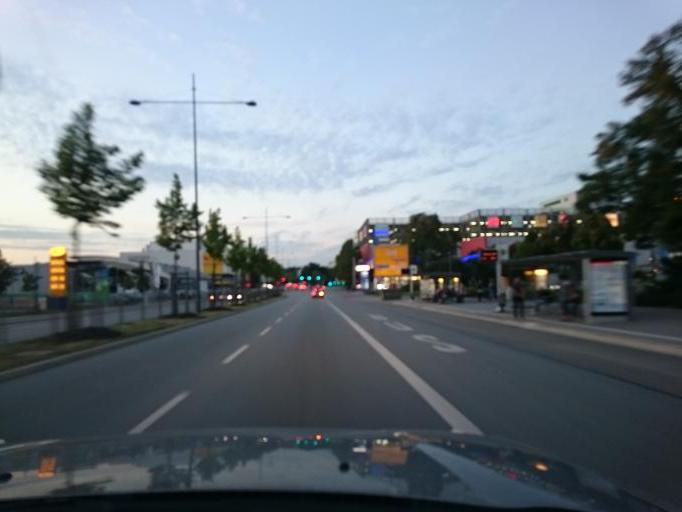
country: DE
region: Bavaria
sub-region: Upper Palatinate
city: Regensburg
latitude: 49.0254
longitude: 12.1139
